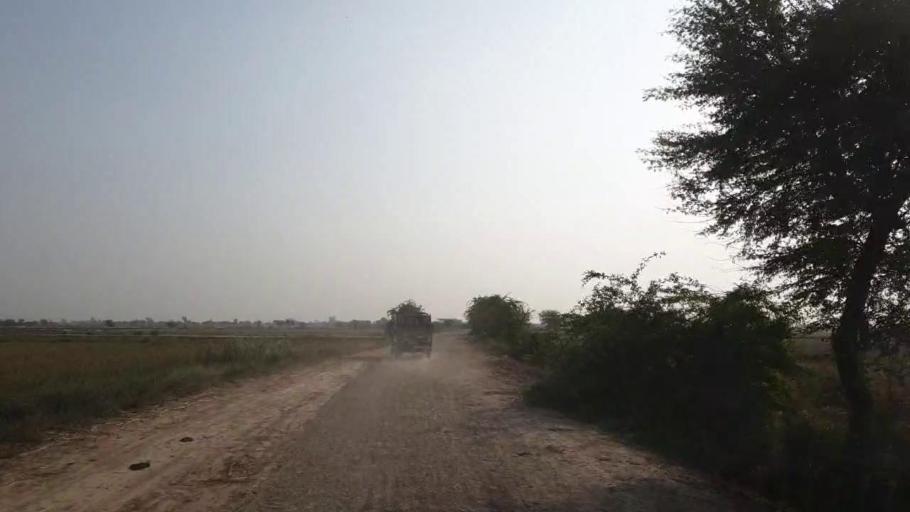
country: PK
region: Sindh
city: Kario
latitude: 24.9075
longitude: 68.5685
